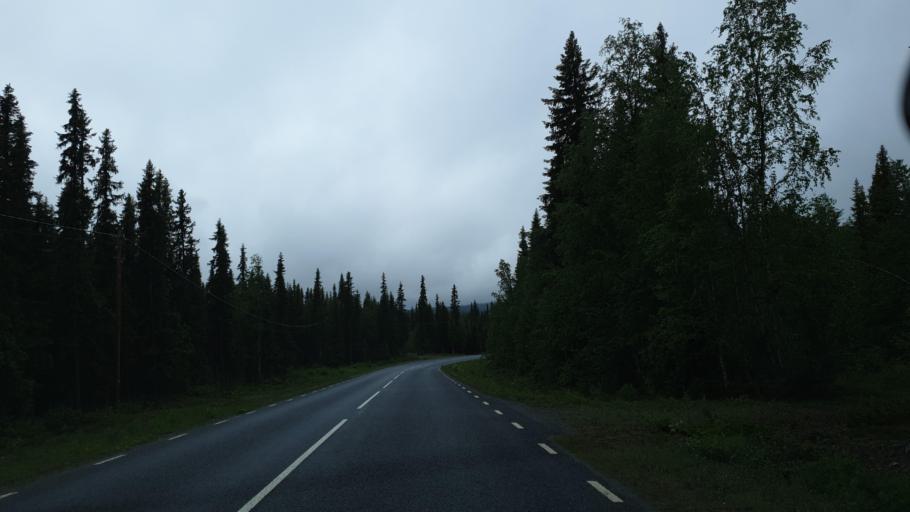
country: SE
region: Vaesterbotten
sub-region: Vilhelmina Kommun
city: Sjoberg
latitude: 65.2283
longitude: 15.9703
